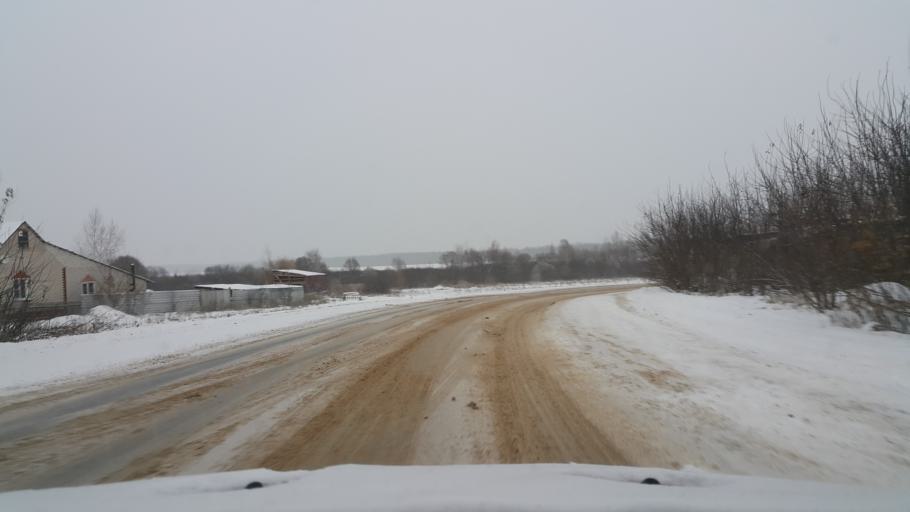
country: RU
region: Tambov
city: Pokrovo-Prigorodnoye
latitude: 52.6607
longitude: 41.4336
